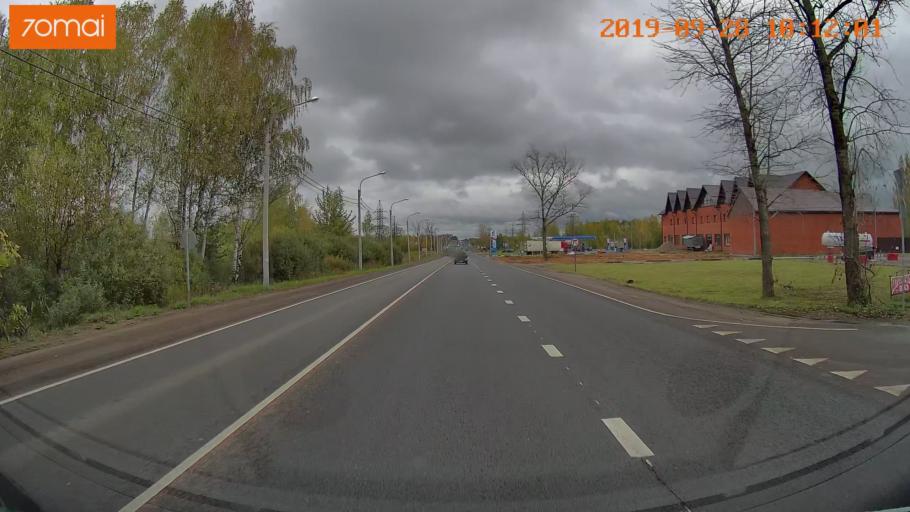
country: RU
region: Jaroslavl
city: Yaroslavl
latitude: 57.5427
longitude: 39.9488
